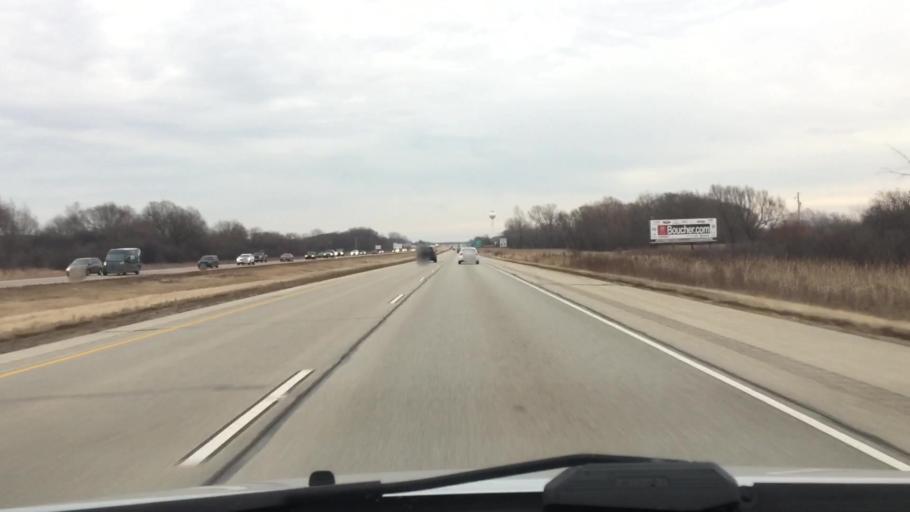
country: US
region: Wisconsin
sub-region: Waukesha County
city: Pewaukee
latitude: 43.1001
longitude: -88.2967
